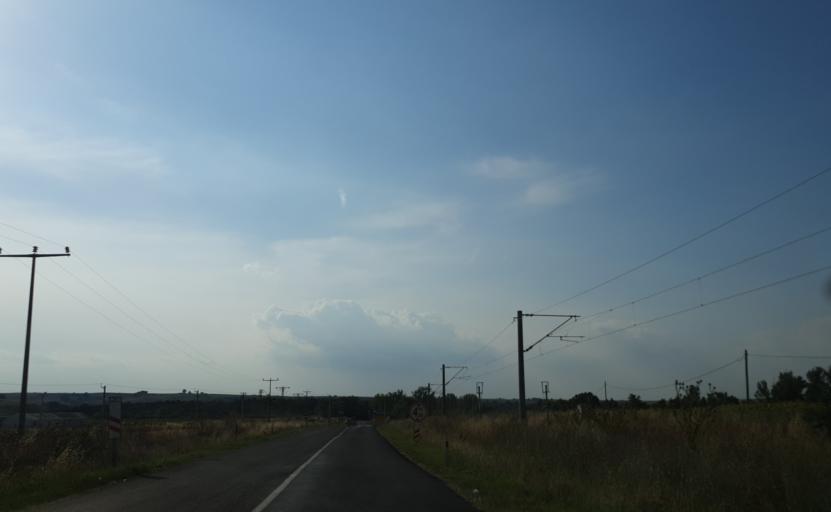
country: TR
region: Tekirdag
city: Muratli
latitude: 41.1812
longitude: 27.4845
